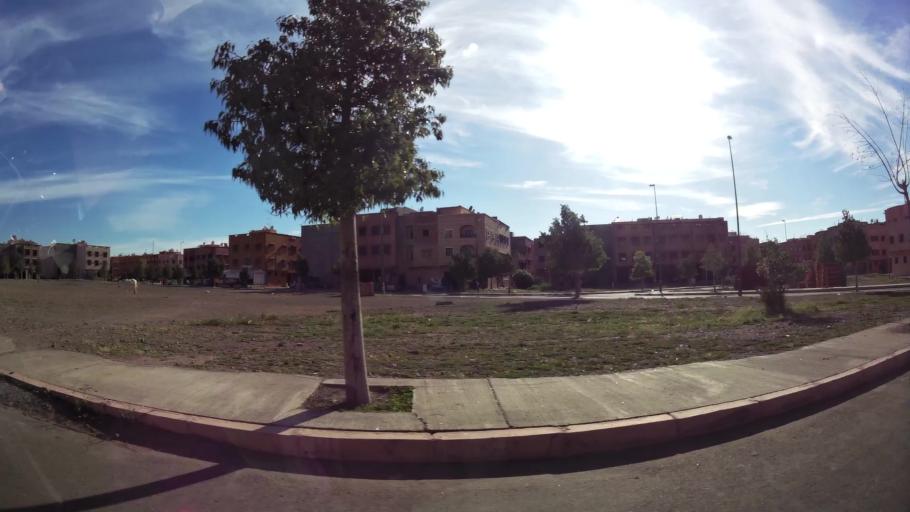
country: MA
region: Marrakech-Tensift-Al Haouz
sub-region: Marrakech
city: Marrakesh
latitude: 31.6871
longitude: -8.0723
